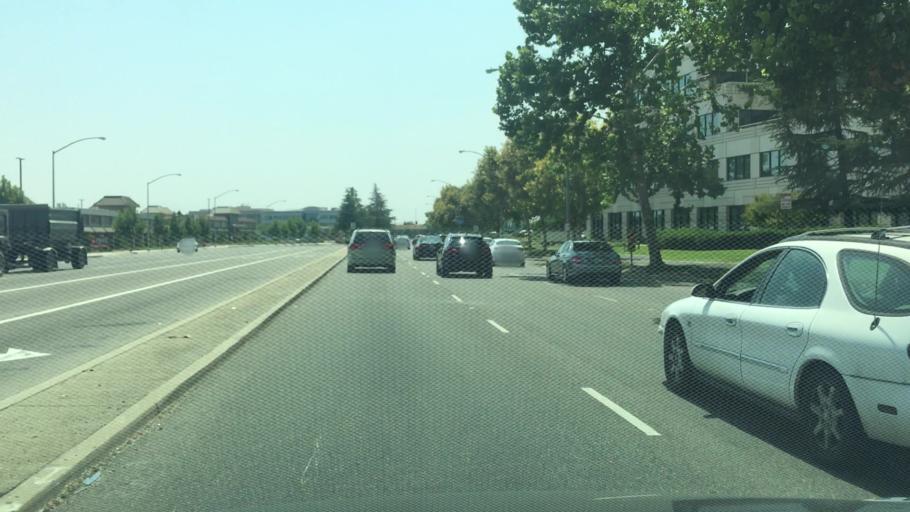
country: US
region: California
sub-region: Fresno County
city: Clovis
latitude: 36.8603
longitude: -119.7829
